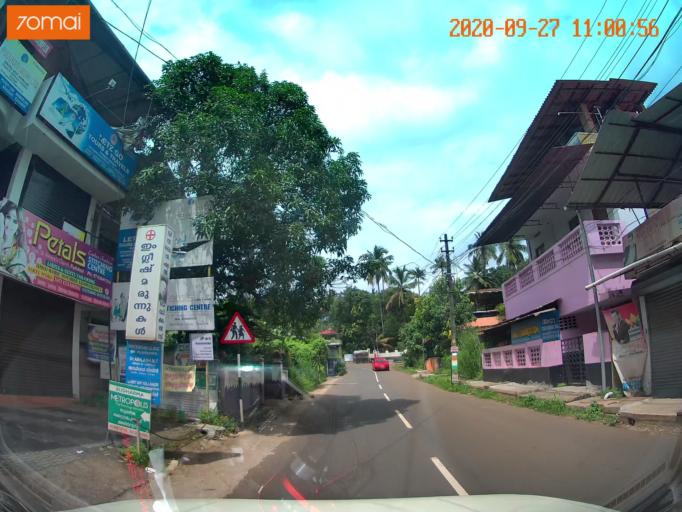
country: IN
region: Kerala
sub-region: Thrissur District
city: Irinjalakuda
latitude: 10.4216
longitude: 76.2677
